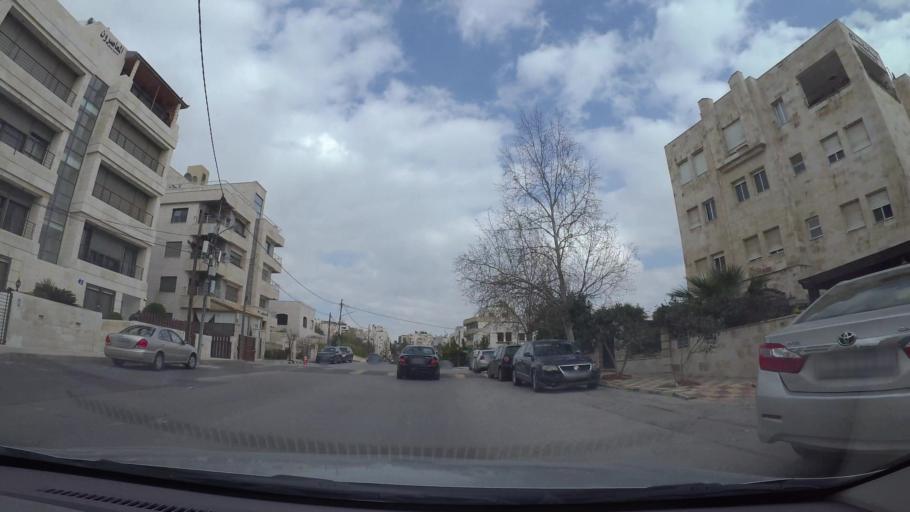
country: JO
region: Amman
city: Wadi as Sir
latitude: 31.9852
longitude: 35.8415
